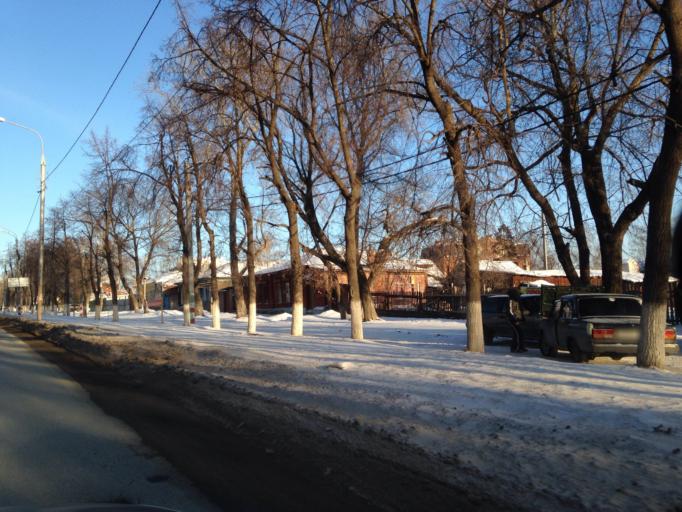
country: RU
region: Ulyanovsk
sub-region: Ulyanovskiy Rayon
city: Ulyanovsk
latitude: 54.3025
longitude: 48.3853
